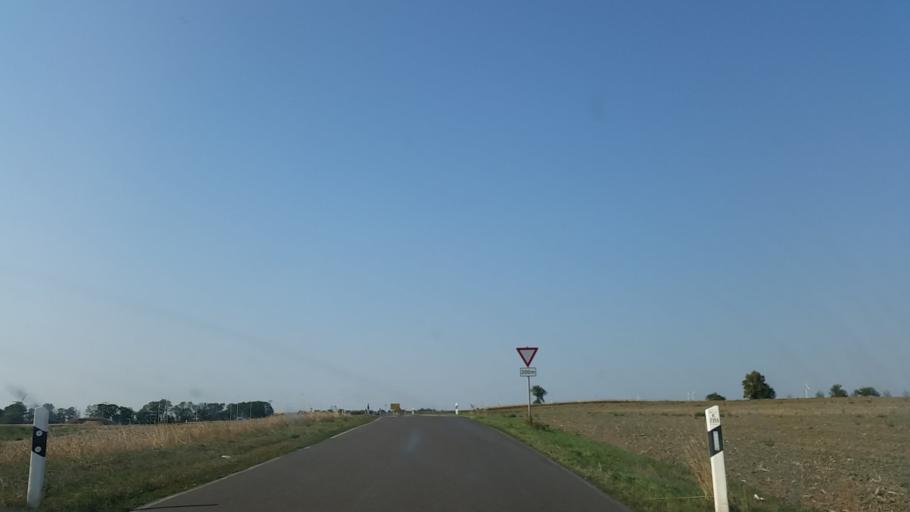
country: DE
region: Brandenburg
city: Pinnow
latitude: 53.0280
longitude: 14.0833
